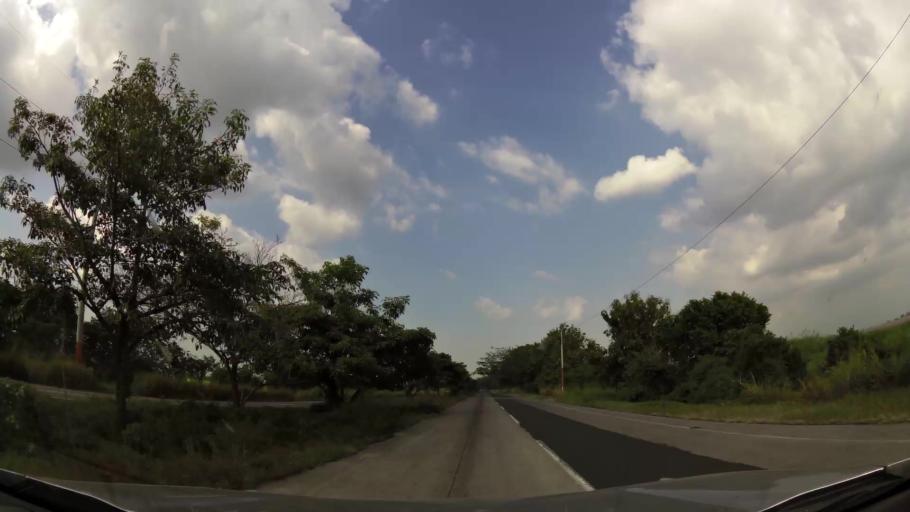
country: GT
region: Escuintla
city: Puerto San Jose
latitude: 14.0485
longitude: -90.7771
